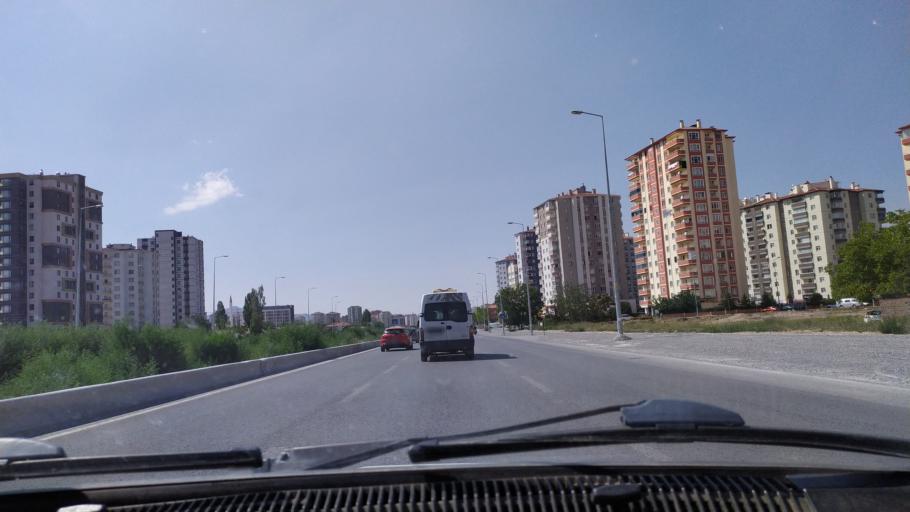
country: TR
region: Kayseri
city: Talas
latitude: 38.7217
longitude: 35.5355
